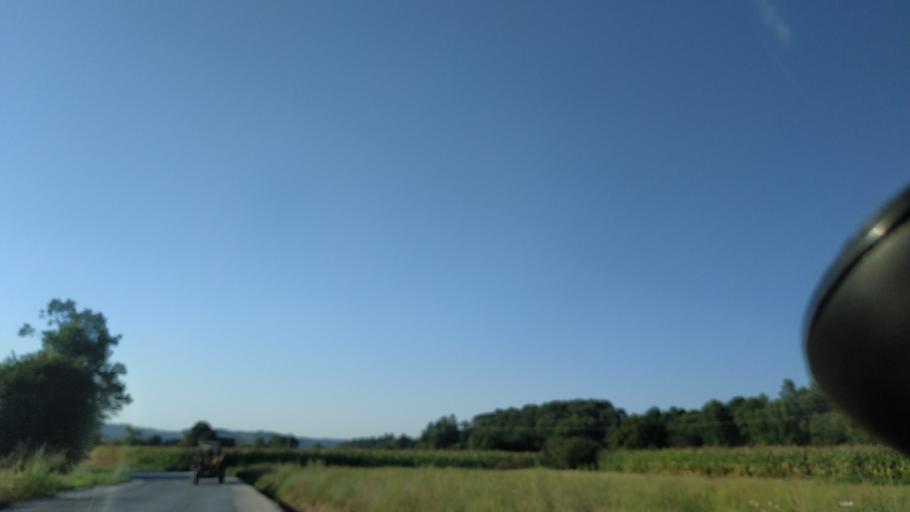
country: RS
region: Central Serbia
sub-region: Rasinski Okrug
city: Krusevac
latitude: 43.5058
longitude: 21.3350
